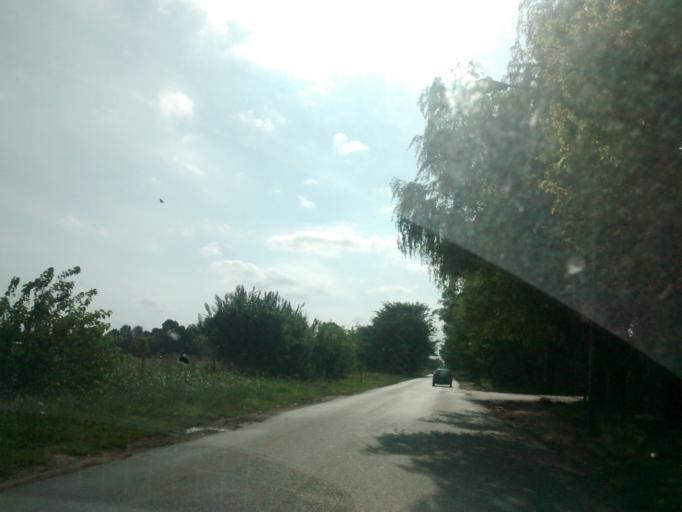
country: AR
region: Buenos Aires
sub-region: Partido de La Plata
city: La Plata
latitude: -34.9599
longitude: -57.8900
